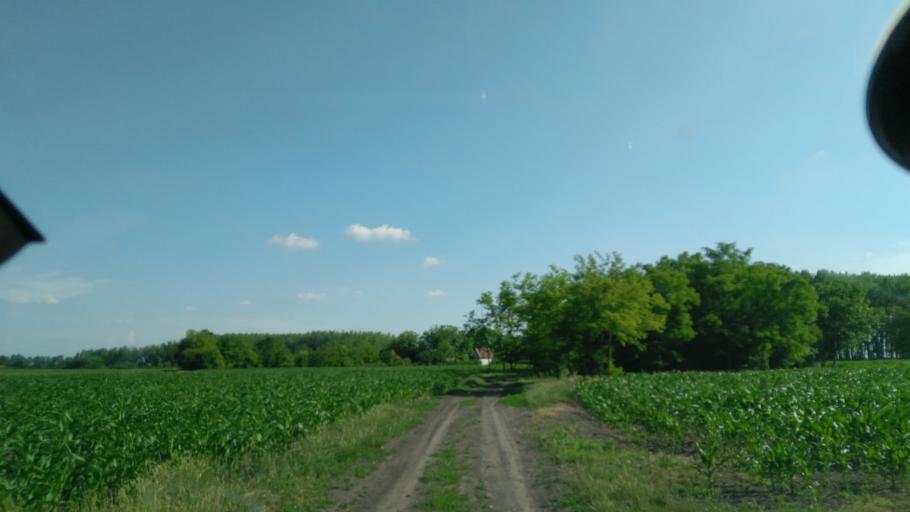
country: HU
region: Bekes
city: Doboz
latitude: 46.7044
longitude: 21.2329
